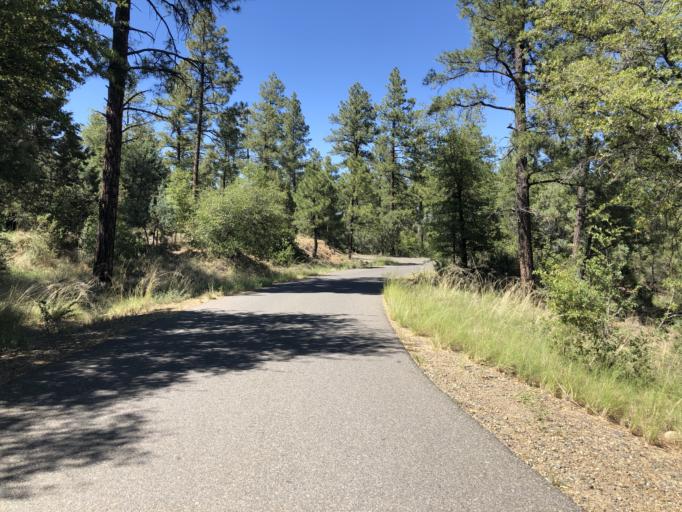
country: US
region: Arizona
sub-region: Yavapai County
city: Prescott
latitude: 34.5164
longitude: -112.3896
